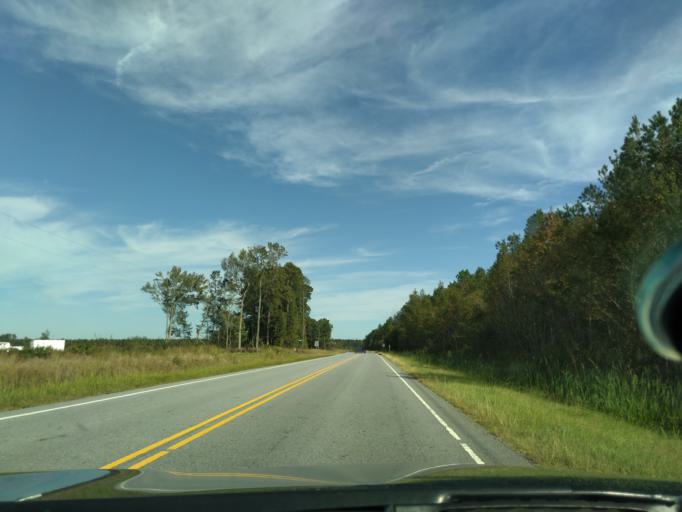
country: US
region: North Carolina
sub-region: Beaufort County
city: River Road
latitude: 35.5244
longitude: -76.8858
